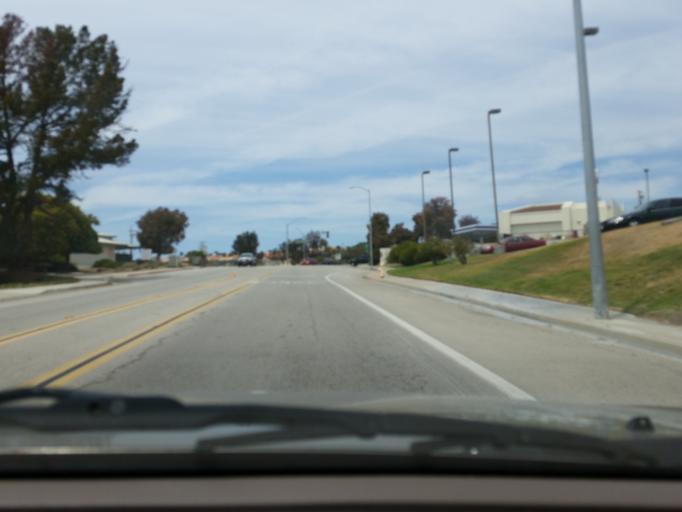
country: US
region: California
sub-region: San Luis Obispo County
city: Grover Beach
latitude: 35.1342
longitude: -120.6222
